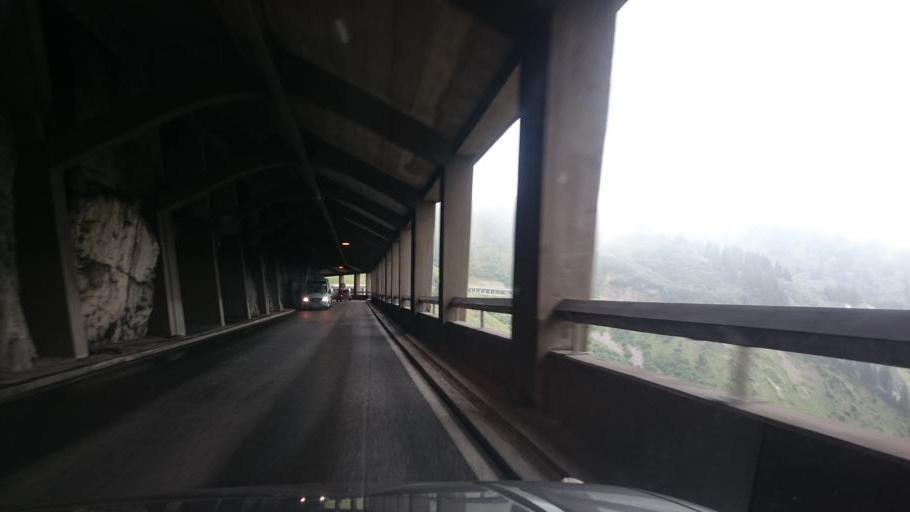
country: AT
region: Vorarlberg
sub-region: Politischer Bezirk Bludenz
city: Lech
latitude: 47.1495
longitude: 10.1659
